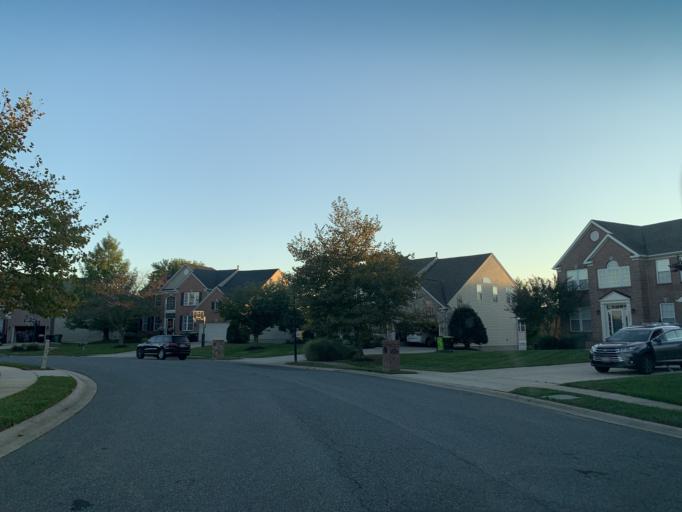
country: US
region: Maryland
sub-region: Harford County
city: Bel Air South
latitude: 39.5288
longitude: -76.3013
